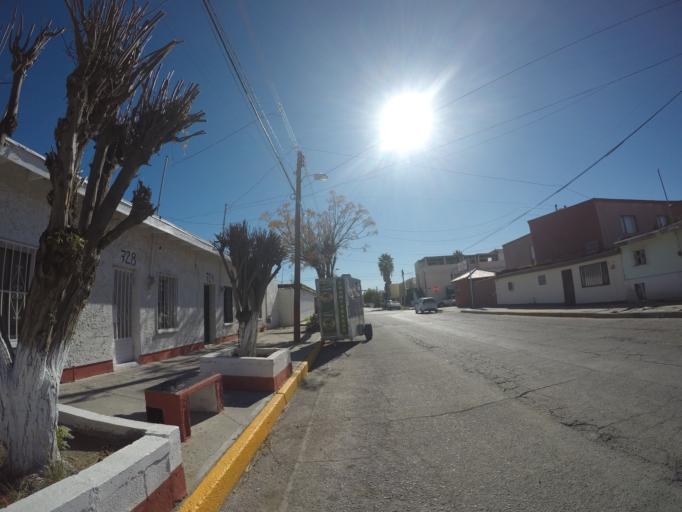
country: MX
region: Chihuahua
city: Ciudad Juarez
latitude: 31.7436
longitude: -106.4607
